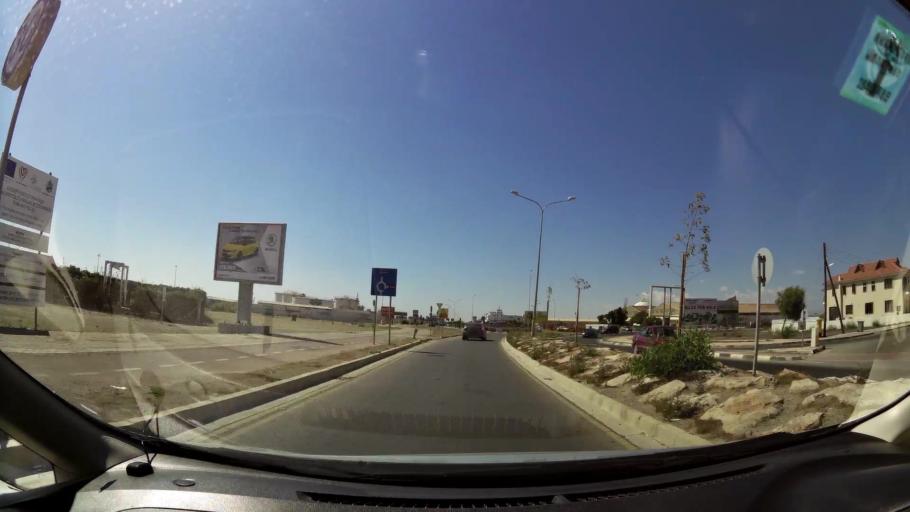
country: CY
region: Larnaka
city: Livadia
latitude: 34.9524
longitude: 33.6501
